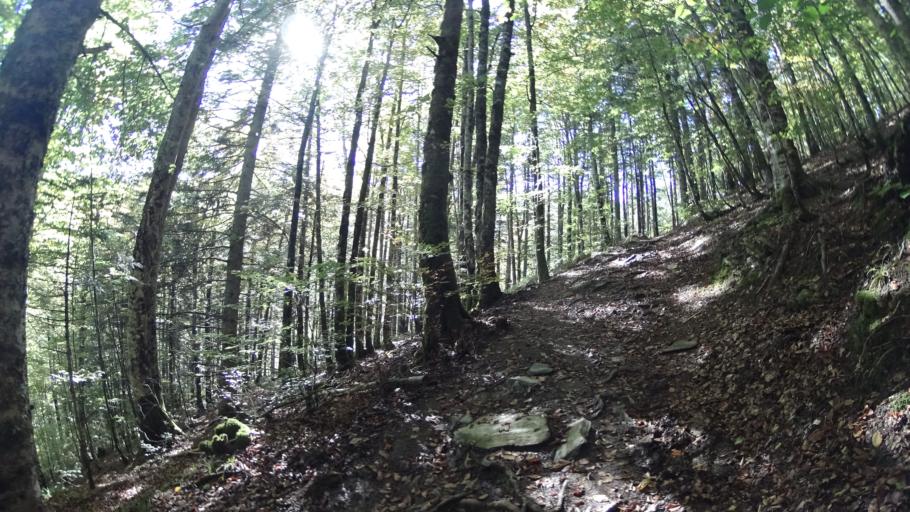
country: ES
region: Navarre
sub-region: Provincia de Navarra
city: Oronz
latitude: 42.9866
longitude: -1.1105
